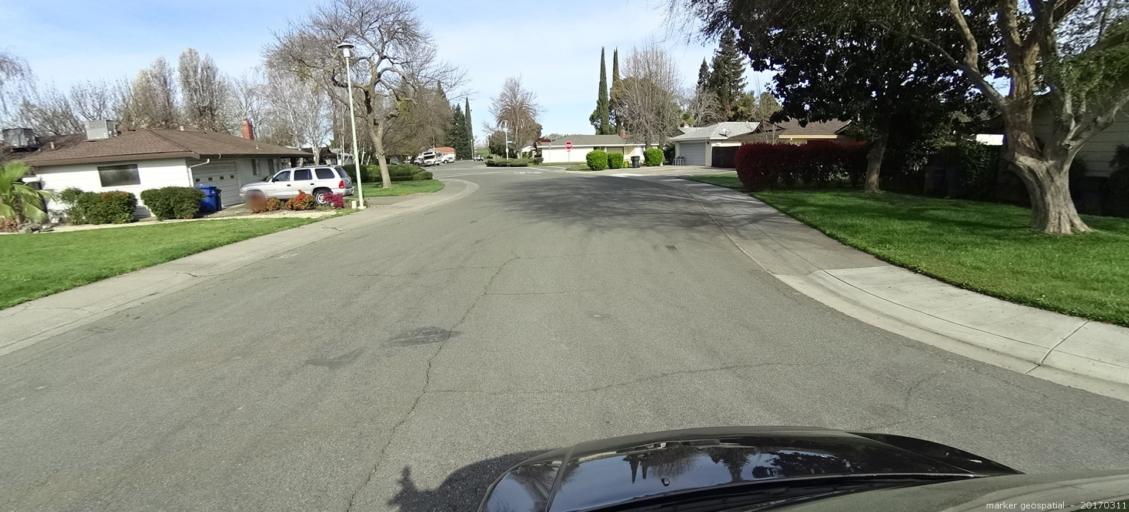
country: US
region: California
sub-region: Yolo County
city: West Sacramento
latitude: 38.5061
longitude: -121.5531
